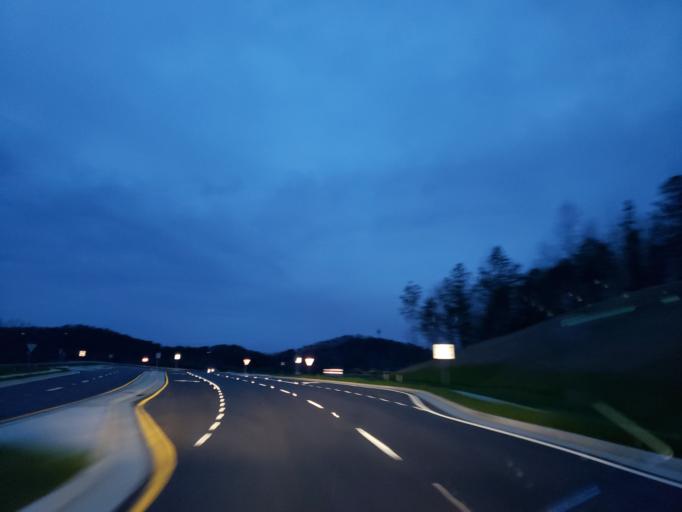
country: US
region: Georgia
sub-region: Bartow County
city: Emerson
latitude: 34.1388
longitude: -84.7446
